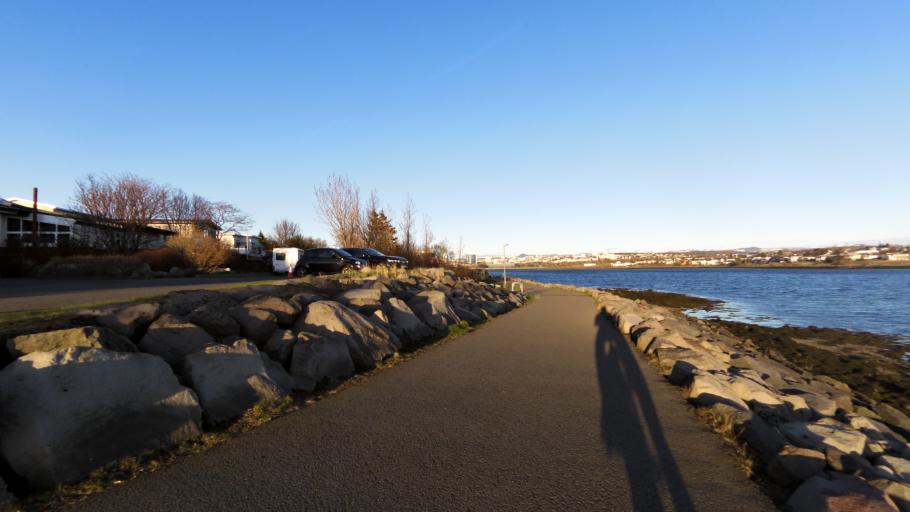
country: IS
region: Capital Region
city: Kopavogur
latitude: 64.1078
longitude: -21.9330
